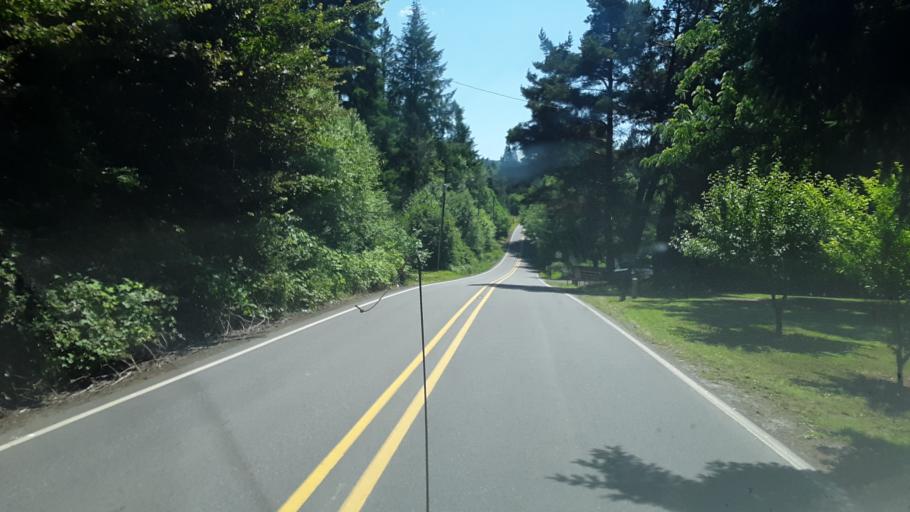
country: US
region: Washington
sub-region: Clark County
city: Amboy
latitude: 45.9059
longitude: -122.4520
